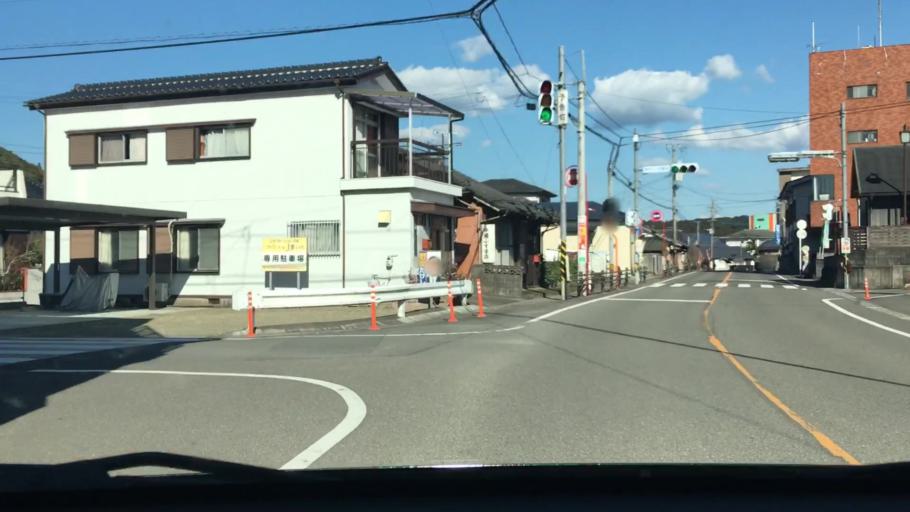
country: JP
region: Kagoshima
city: Satsumasendai
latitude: 31.7878
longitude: 130.4040
